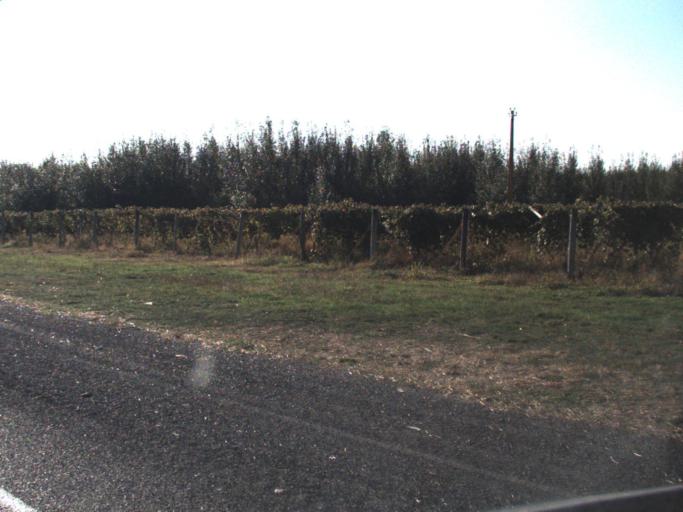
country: US
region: Washington
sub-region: Walla Walla County
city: Burbank
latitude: 46.2204
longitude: -118.8669
